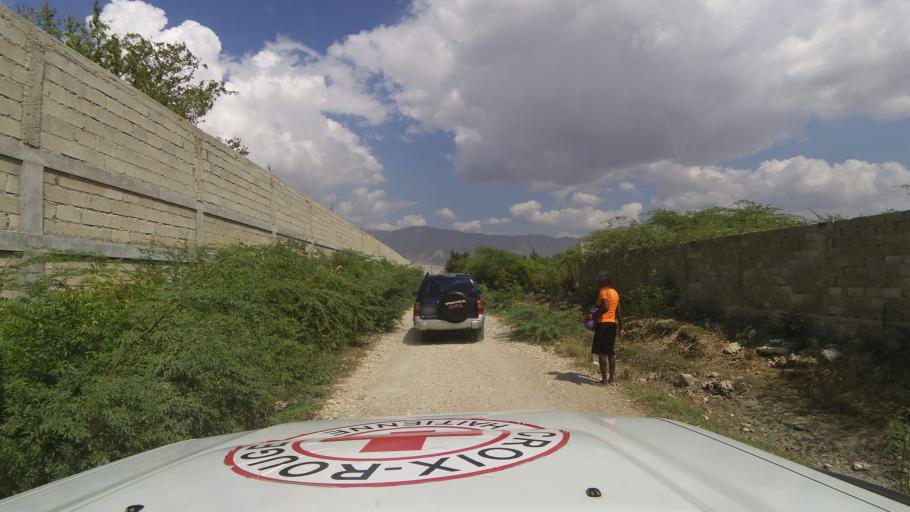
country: HT
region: Ouest
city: Croix des Bouquets
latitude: 18.6410
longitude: -72.2671
